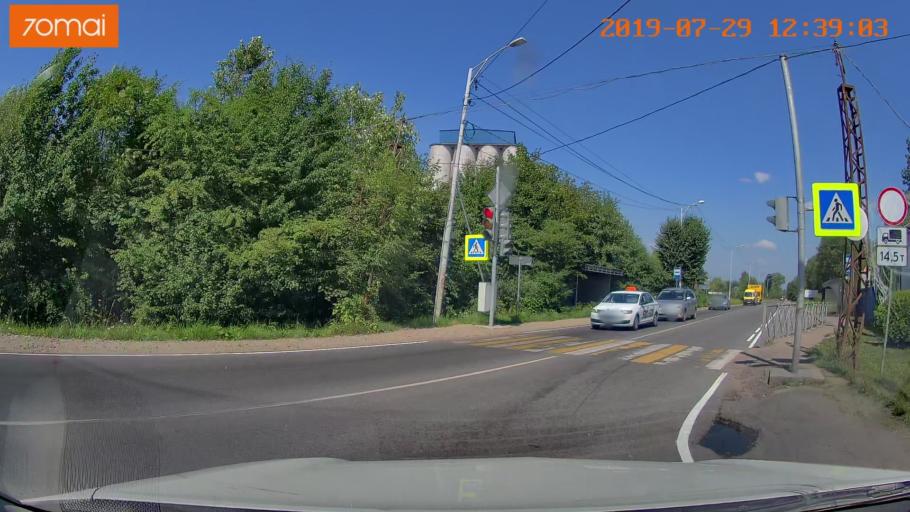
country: RU
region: Kaliningrad
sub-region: Gorod Kaliningrad
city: Kaliningrad
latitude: 54.6568
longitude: 20.5422
